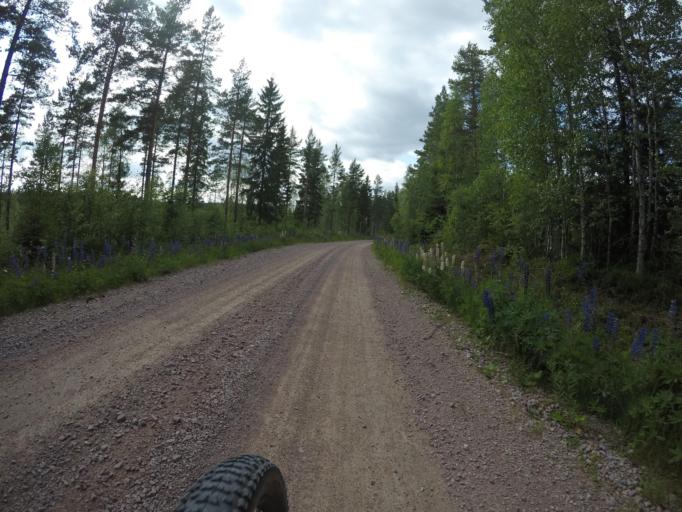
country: SE
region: Dalarna
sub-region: Ludvika Kommun
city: Abborrberget
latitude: 60.1077
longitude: 14.4846
